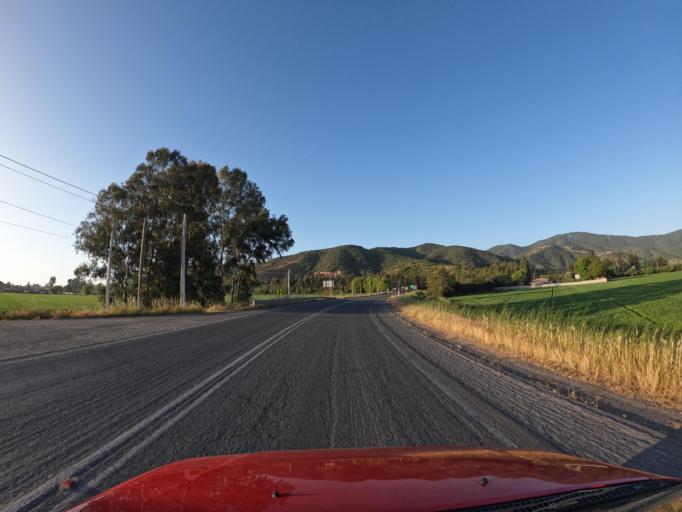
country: CL
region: O'Higgins
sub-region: Provincia de Cachapoal
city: San Vicente
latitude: -34.2742
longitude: -71.3630
